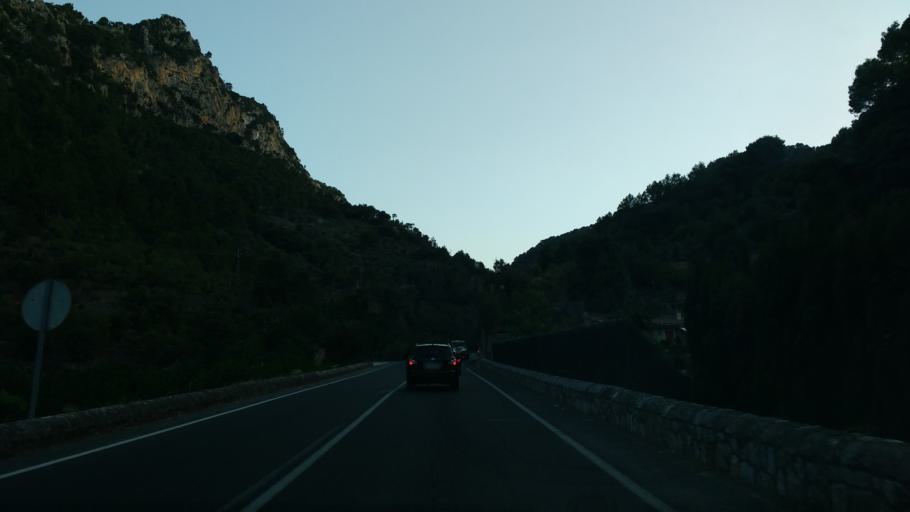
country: ES
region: Balearic Islands
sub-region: Illes Balears
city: Soller
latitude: 39.7509
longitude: 2.7045
